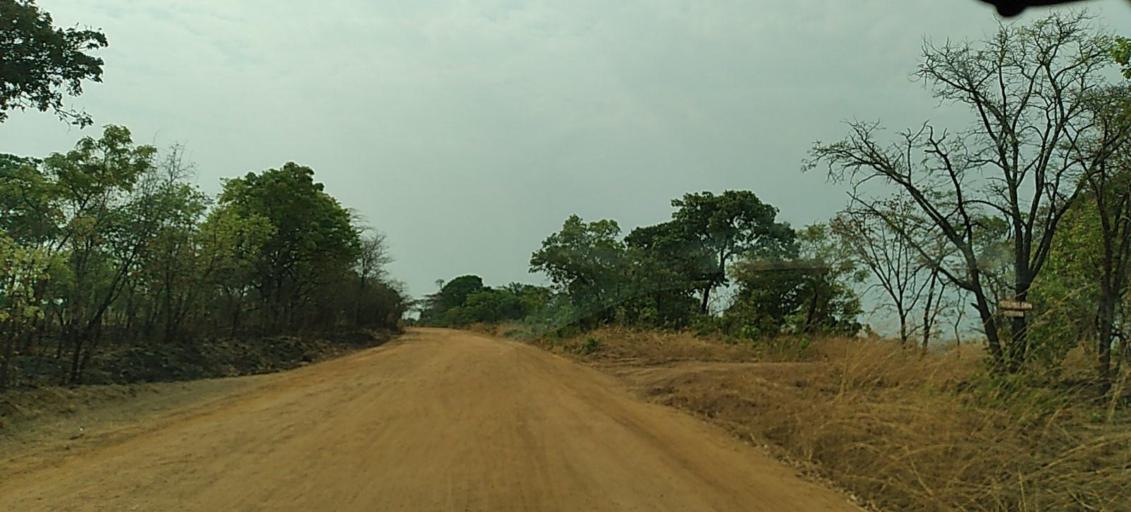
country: ZM
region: North-Western
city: Kabompo
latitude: -13.4235
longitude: 24.4021
